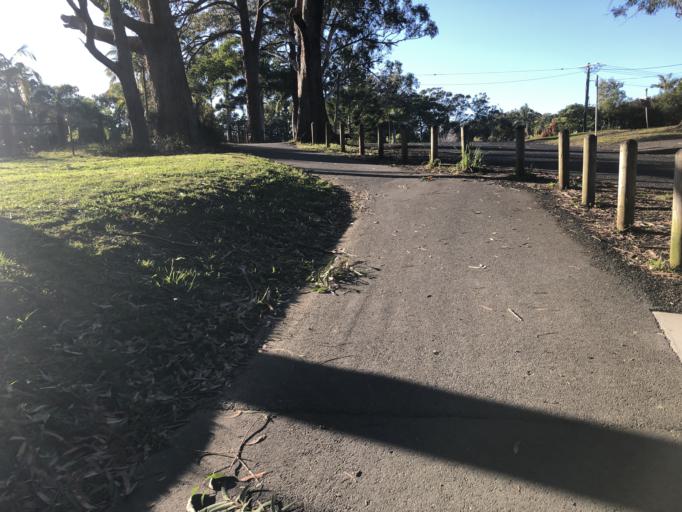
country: AU
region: New South Wales
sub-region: Coffs Harbour
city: Coffs Harbour
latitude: -30.2980
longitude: 153.1218
